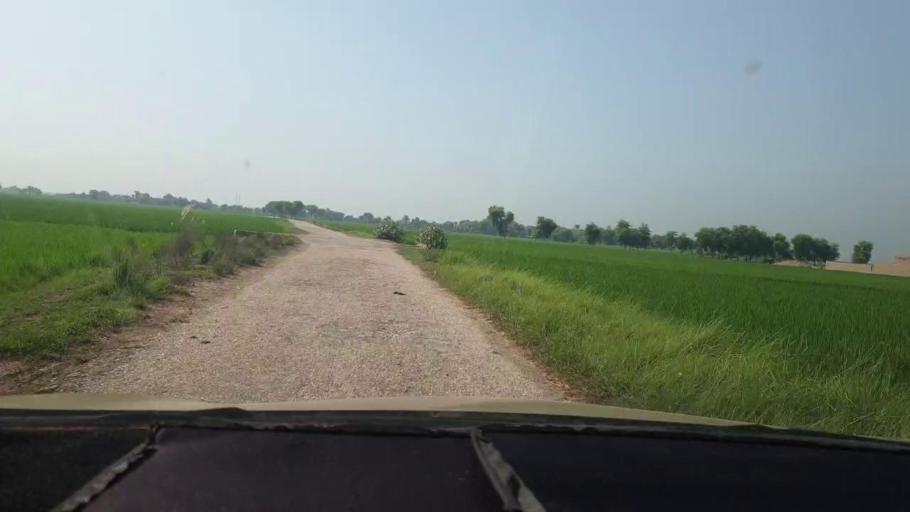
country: PK
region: Sindh
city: Kambar
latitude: 27.5760
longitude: 68.0556
